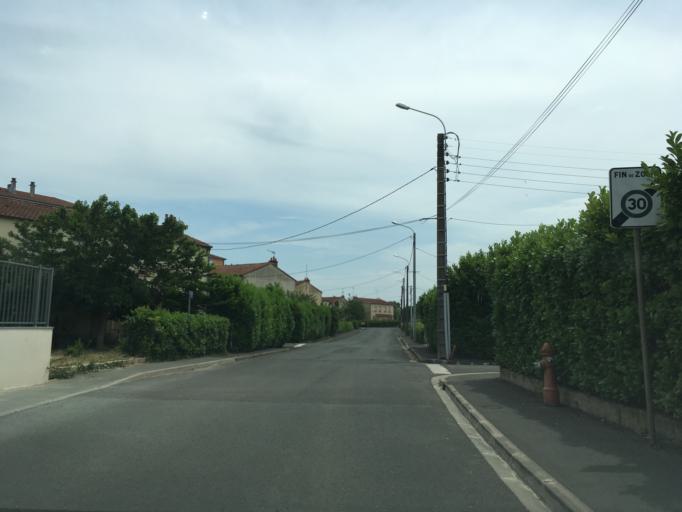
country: FR
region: Poitou-Charentes
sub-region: Departement des Deux-Sevres
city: Niort
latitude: 46.3243
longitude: -0.4782
